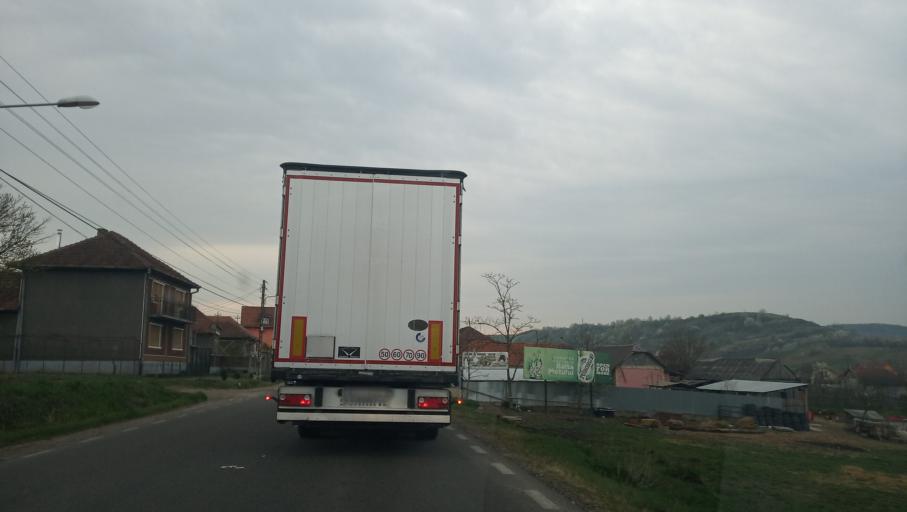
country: RO
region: Bihor
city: Hidiselu de Sus
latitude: 46.9472
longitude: 22.0220
